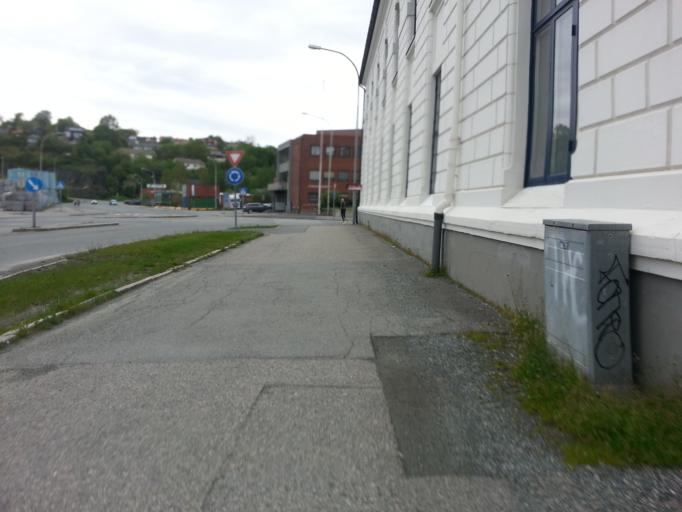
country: NO
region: Sor-Trondelag
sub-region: Trondheim
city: Trondheim
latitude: 63.4417
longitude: 10.4269
